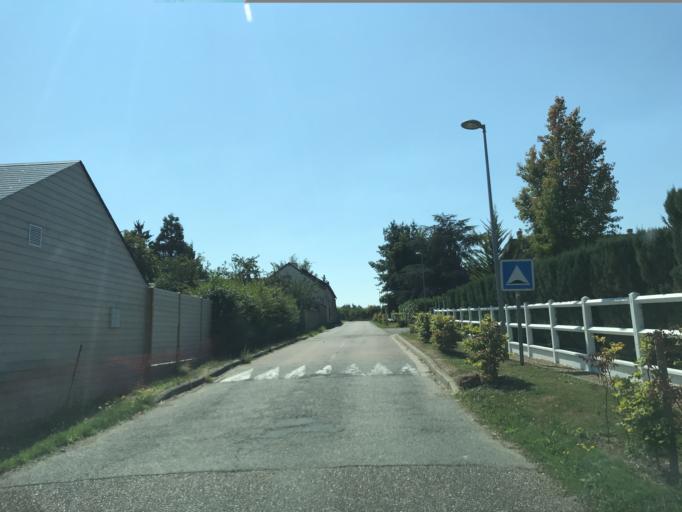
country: FR
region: Haute-Normandie
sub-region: Departement de l'Eure
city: Heudreville-sur-Eure
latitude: 49.0973
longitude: 1.2086
